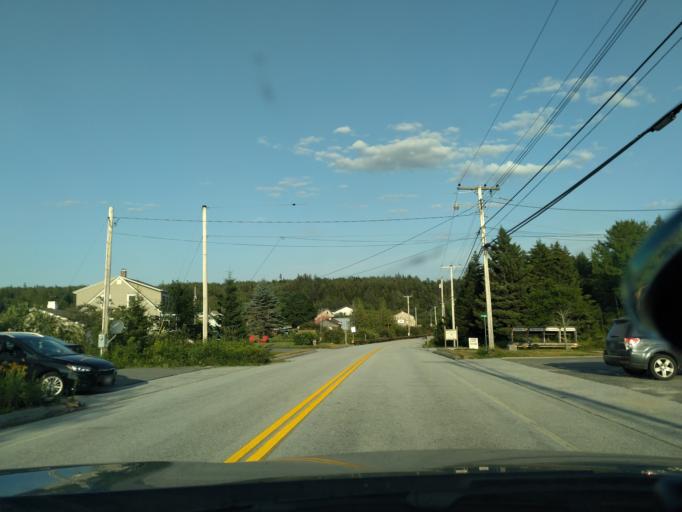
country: US
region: Maine
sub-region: Hancock County
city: Gouldsboro
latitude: 44.3955
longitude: -68.0790
